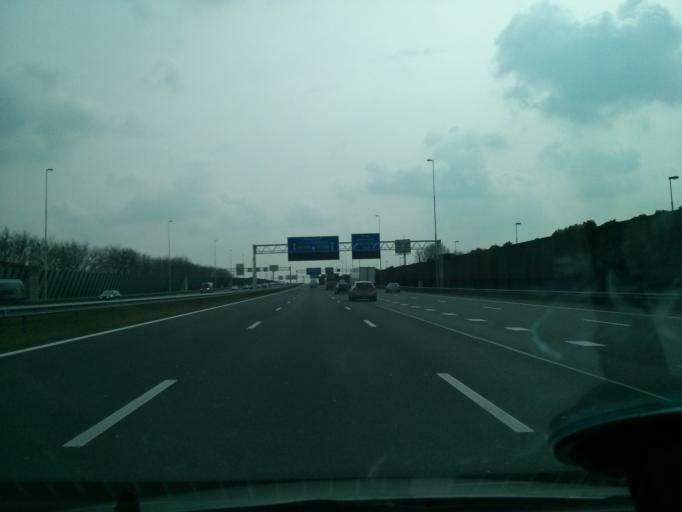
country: NL
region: Utrecht
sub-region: Gemeente Vianen
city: Vianen
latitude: 51.9853
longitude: 5.0877
